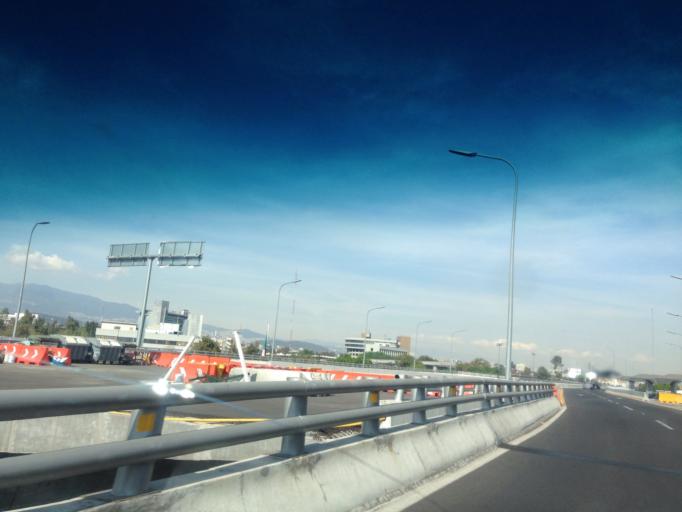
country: MX
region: Mexico City
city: Tlalpan
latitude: 19.2873
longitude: -99.1491
